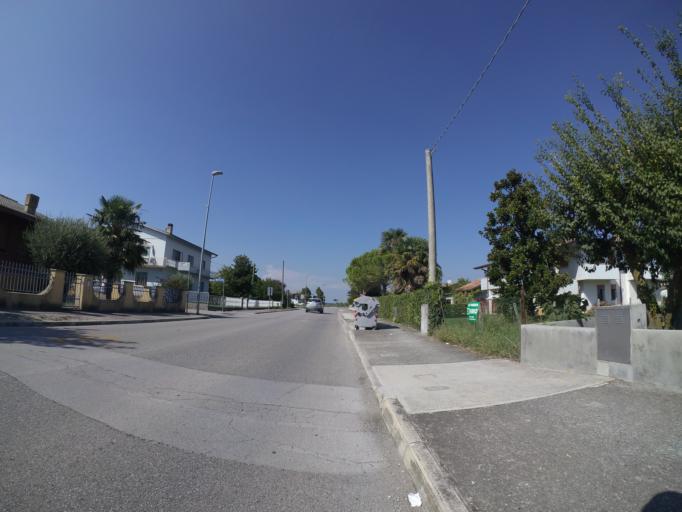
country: IT
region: Friuli Venezia Giulia
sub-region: Provincia di Udine
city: Marano Lagunare
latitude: 45.7722
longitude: 13.1674
